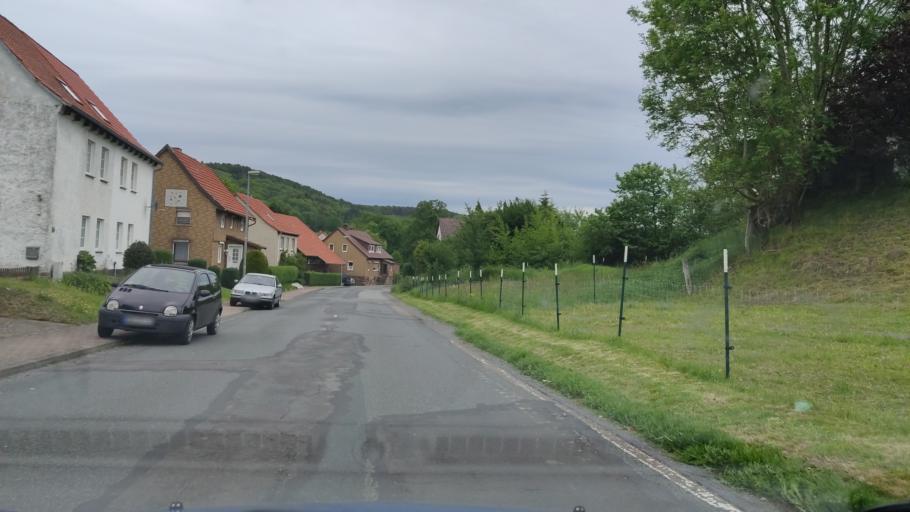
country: DE
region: Lower Saxony
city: Hardegsen
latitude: 51.6906
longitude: 9.8024
